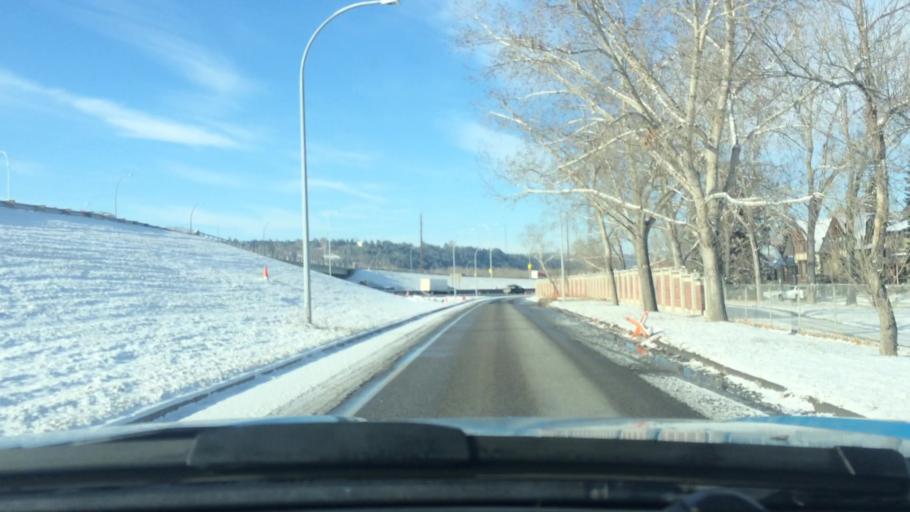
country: CA
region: Alberta
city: Calgary
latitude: 51.0498
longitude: -114.1147
